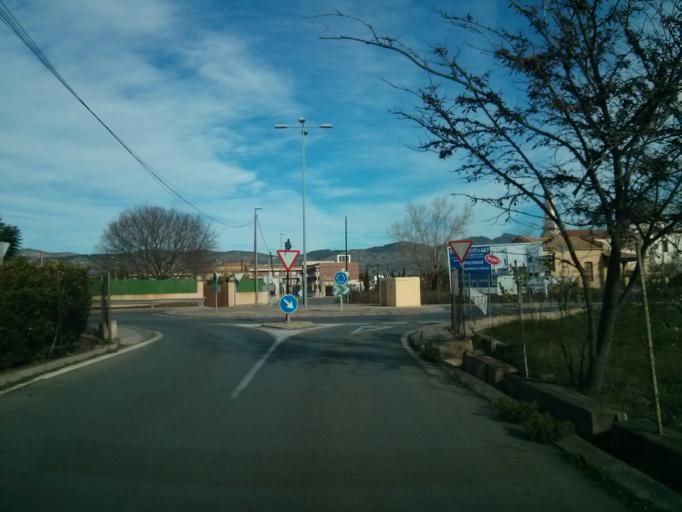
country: ES
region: Valencia
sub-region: Provincia de Castello
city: Castello de la Plana
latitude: 39.9956
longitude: -0.0209
